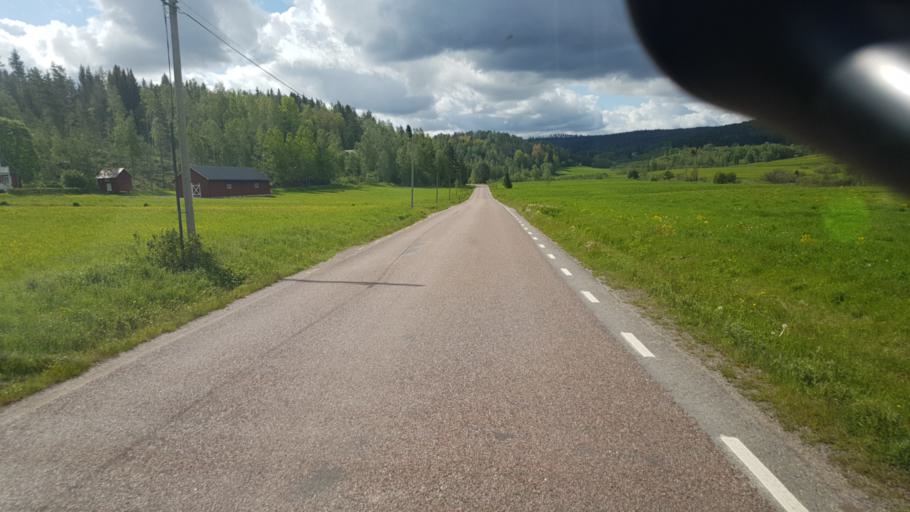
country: NO
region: Ostfold
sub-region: Romskog
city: Romskog
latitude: 59.7066
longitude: 12.0758
